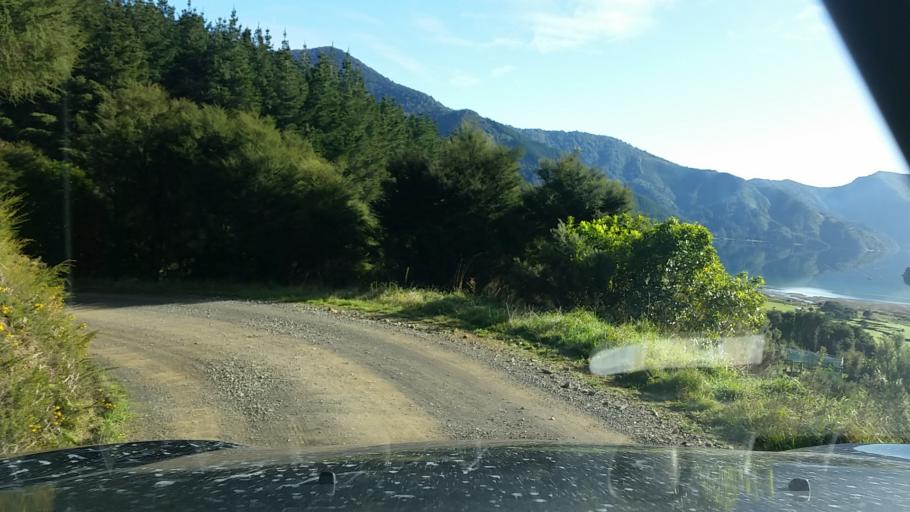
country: NZ
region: Marlborough
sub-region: Marlborough District
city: Picton
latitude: -41.1566
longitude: 173.9710
